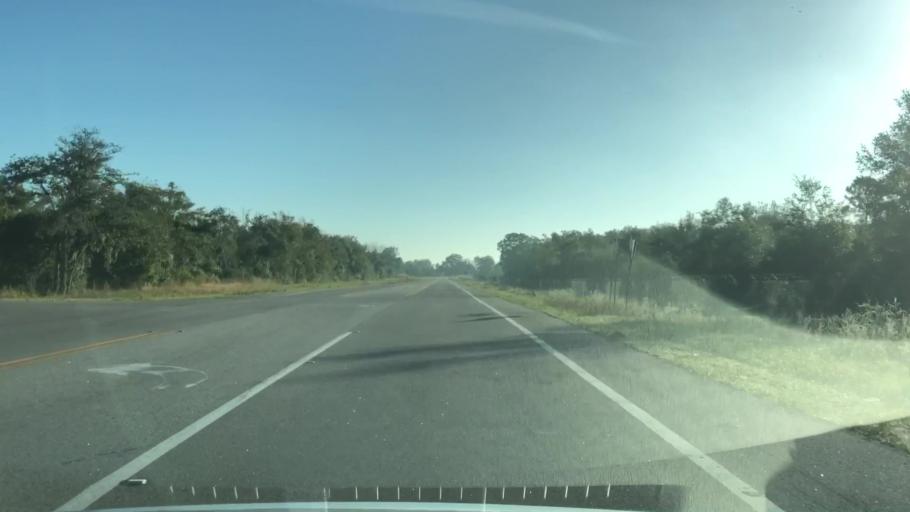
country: US
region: Florida
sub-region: Seminole County
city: Midway
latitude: 28.7856
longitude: -81.2525
